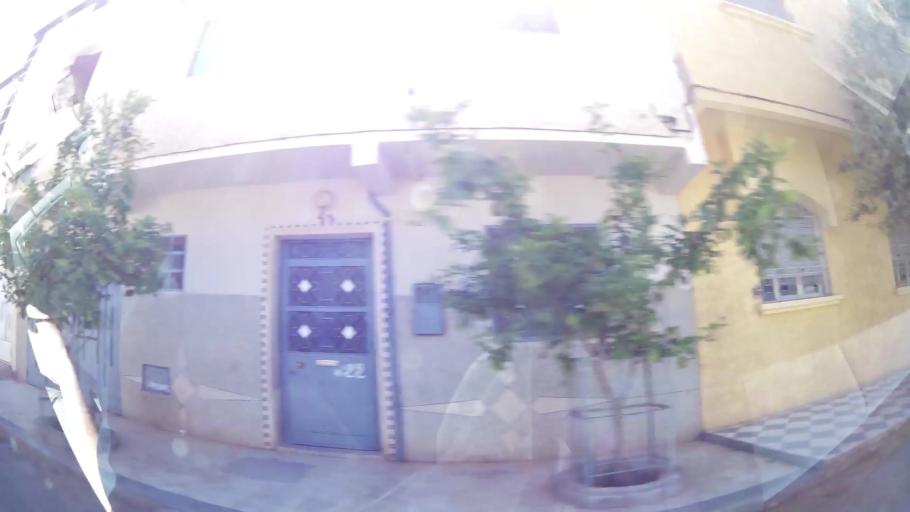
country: MA
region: Oriental
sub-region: Oujda-Angad
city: Oujda
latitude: 34.6688
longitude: -1.8704
